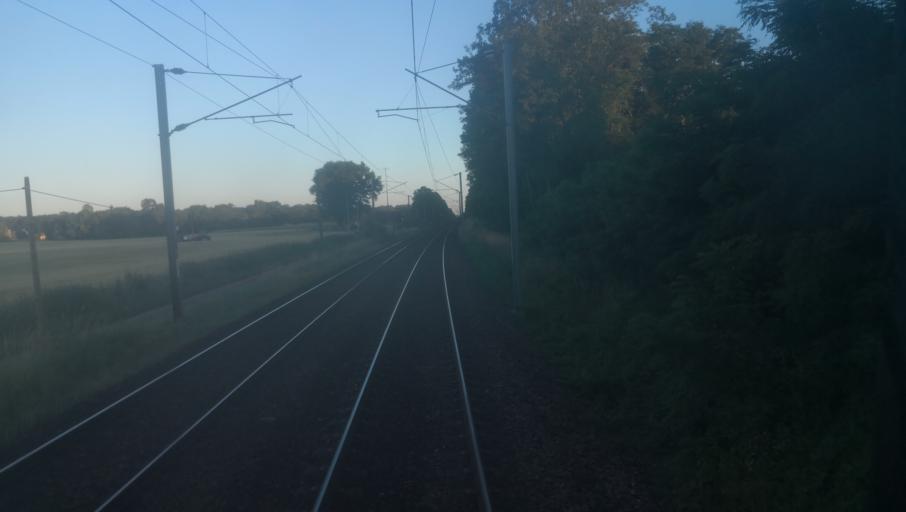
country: FR
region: Bourgogne
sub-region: Departement de la Nievre
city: La Charite-sur-Loire
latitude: 47.2238
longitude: 3.0164
